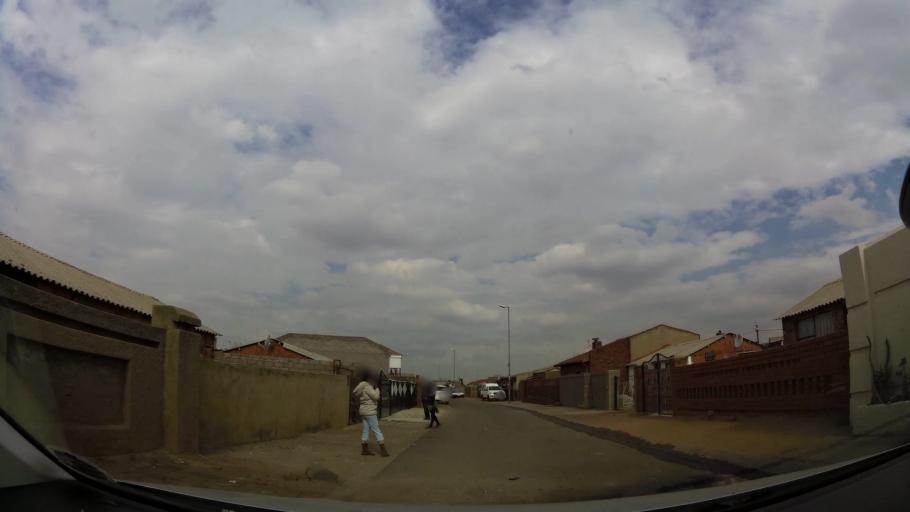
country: ZA
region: Gauteng
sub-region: City of Johannesburg Metropolitan Municipality
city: Soweto
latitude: -26.2658
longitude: 27.8577
